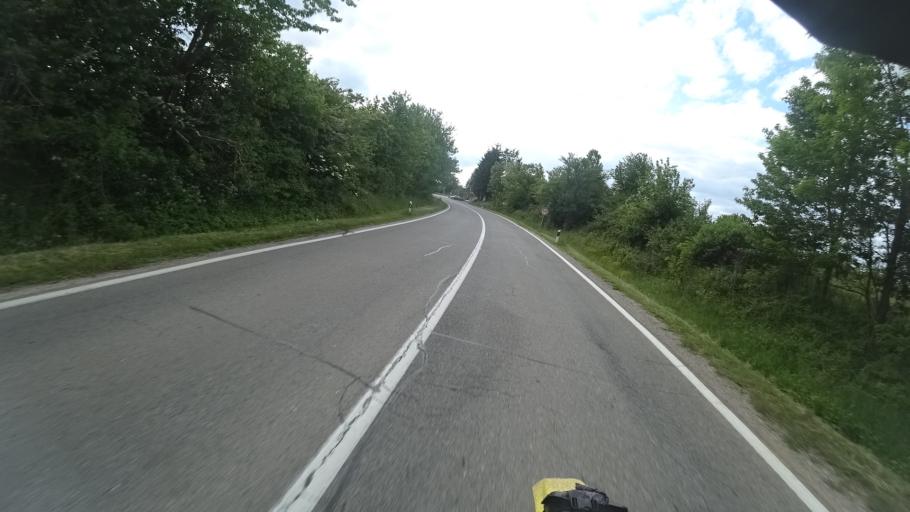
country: HR
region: Licko-Senjska
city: Gospic
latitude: 44.5131
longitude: 15.4256
